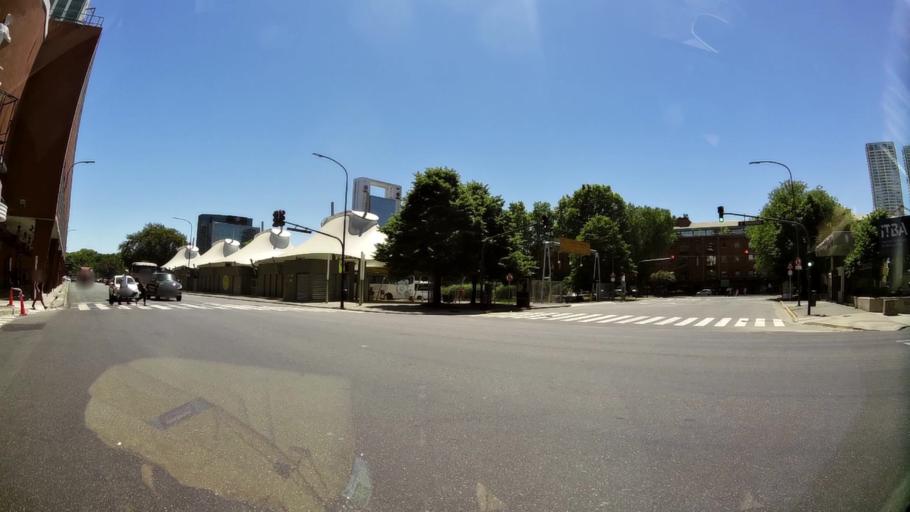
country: AR
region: Buenos Aires F.D.
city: Buenos Aires
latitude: -34.6029
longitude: -58.3682
